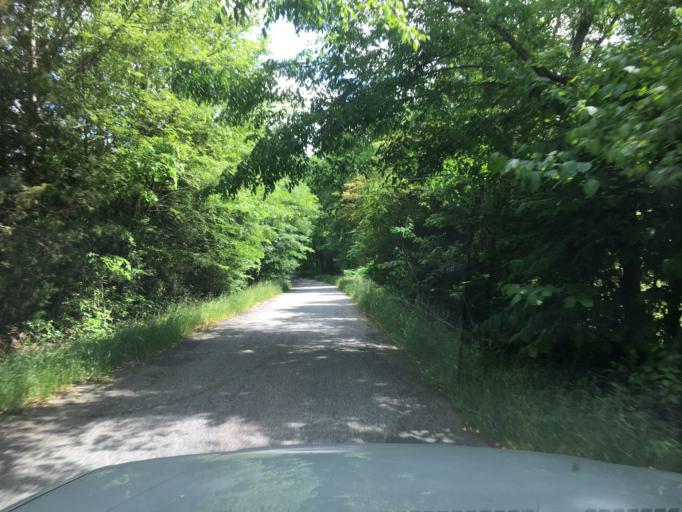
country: US
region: South Carolina
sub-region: Laurens County
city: Watts Mills
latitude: 34.5499
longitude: -81.9448
